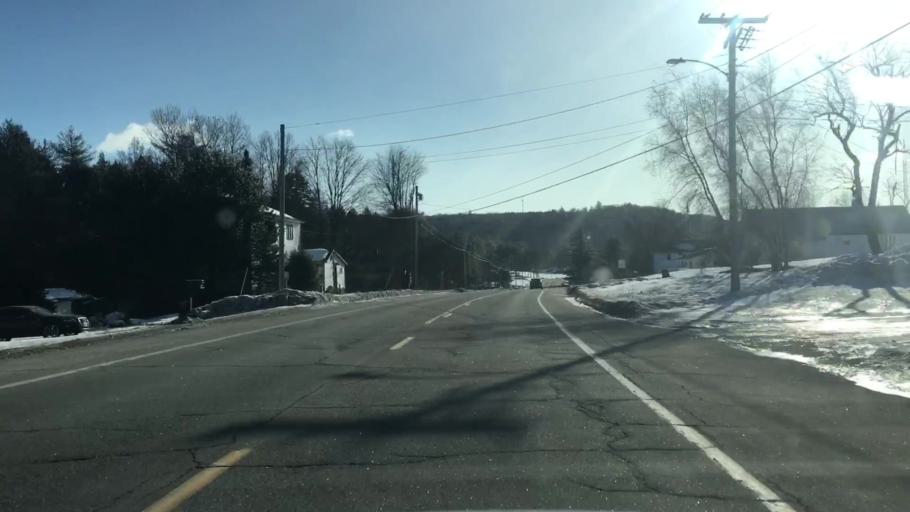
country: US
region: Maine
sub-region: Oxford County
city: West Paris
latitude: 44.3275
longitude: -70.5509
